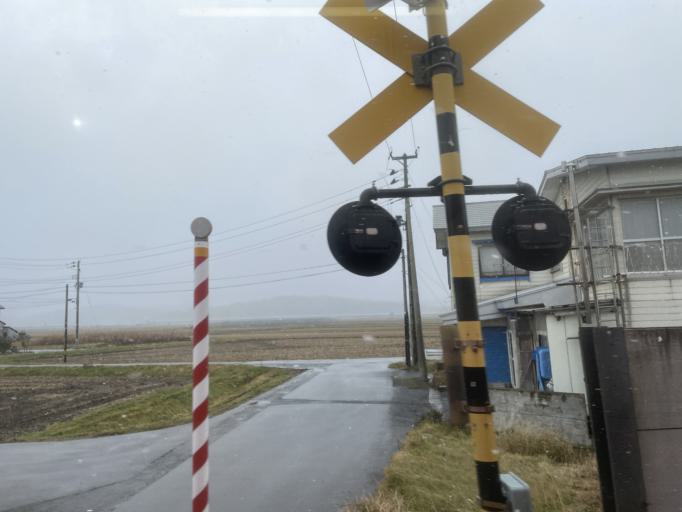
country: JP
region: Aomori
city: Aomori Shi
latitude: 40.9136
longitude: 140.6681
